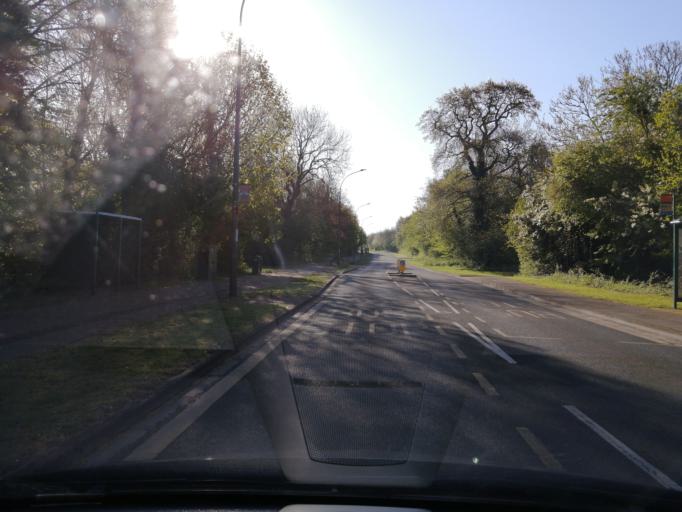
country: GB
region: England
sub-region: Peterborough
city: Castor
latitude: 52.5583
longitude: -0.3131
